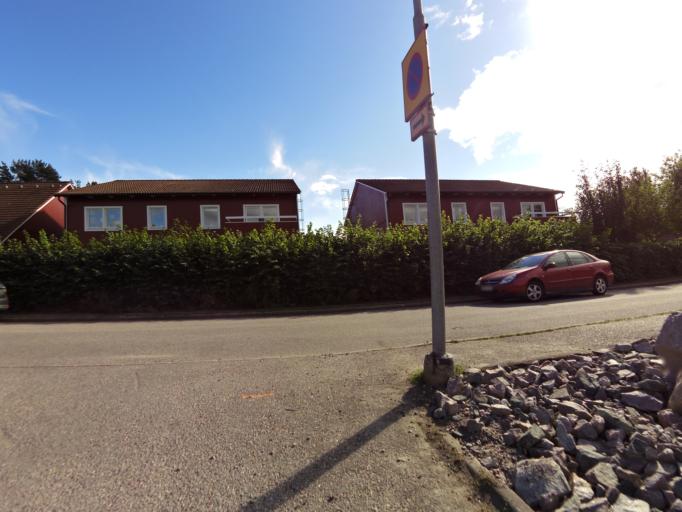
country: SE
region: Gaevleborg
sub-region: Gavle Kommun
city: Gavle
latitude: 60.6634
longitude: 17.2068
